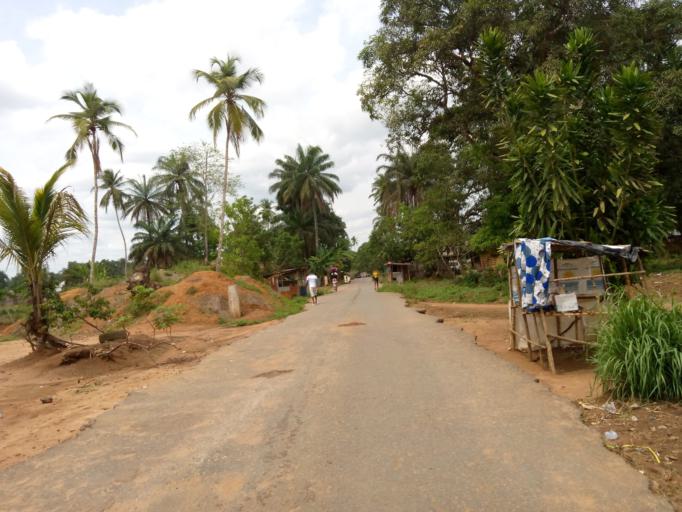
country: SL
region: Western Area
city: Waterloo
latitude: 8.3346
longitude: -13.0087
